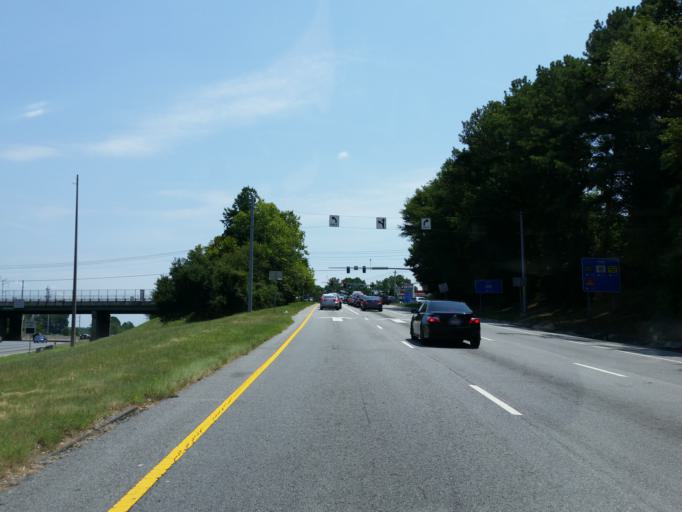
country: US
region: Georgia
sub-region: DeKalb County
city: Dunwoody
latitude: 33.9199
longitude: -84.3168
